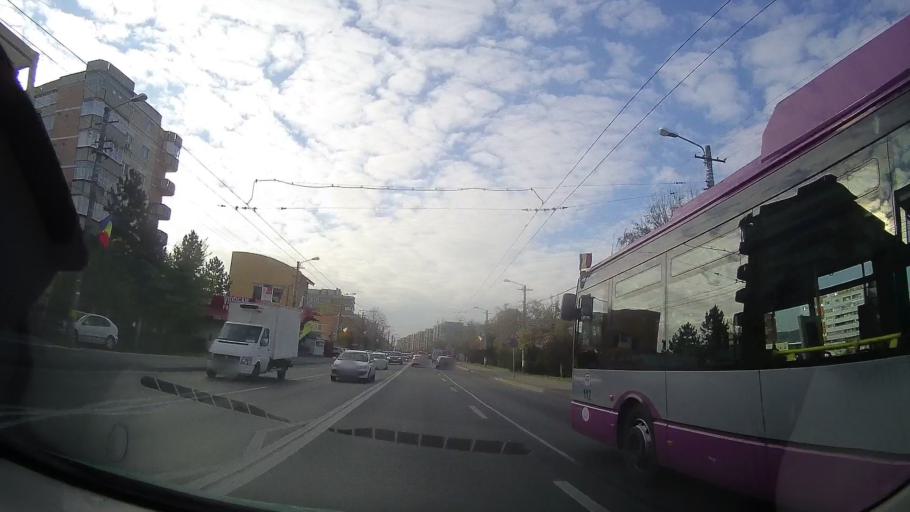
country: RO
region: Cluj
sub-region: Municipiul Cluj-Napoca
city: Cluj-Napoca
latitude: 46.7811
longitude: 23.6301
